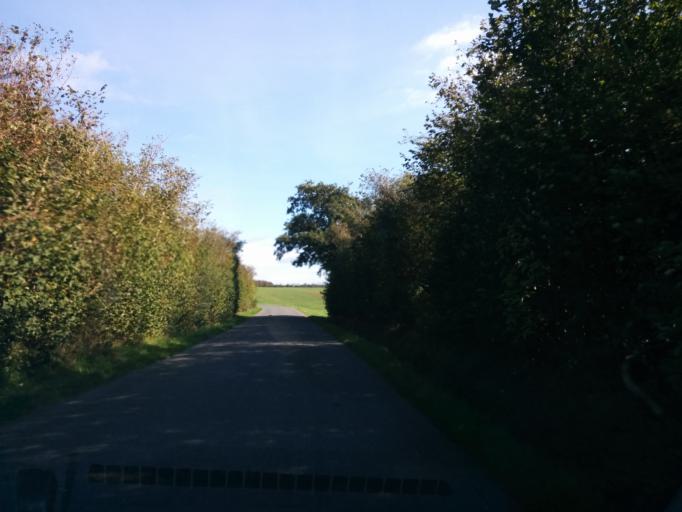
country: DK
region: South Denmark
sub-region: Kolding Kommune
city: Sonder Bjert
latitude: 55.4049
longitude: 9.5646
